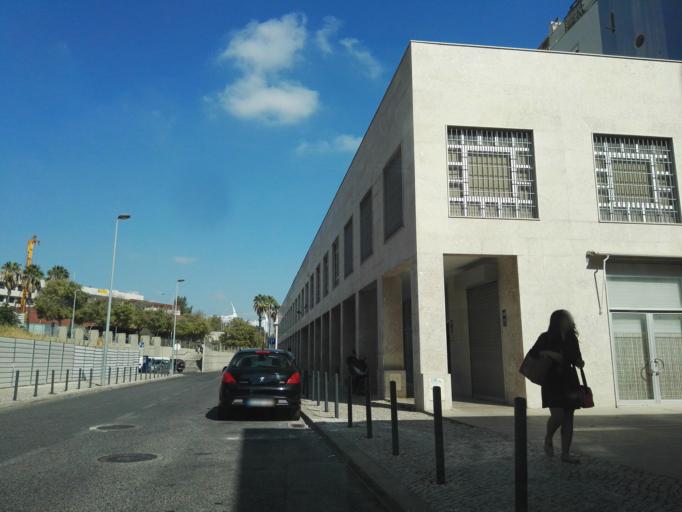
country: PT
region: Lisbon
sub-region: Loures
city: Moscavide
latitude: 38.7571
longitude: -9.0973
